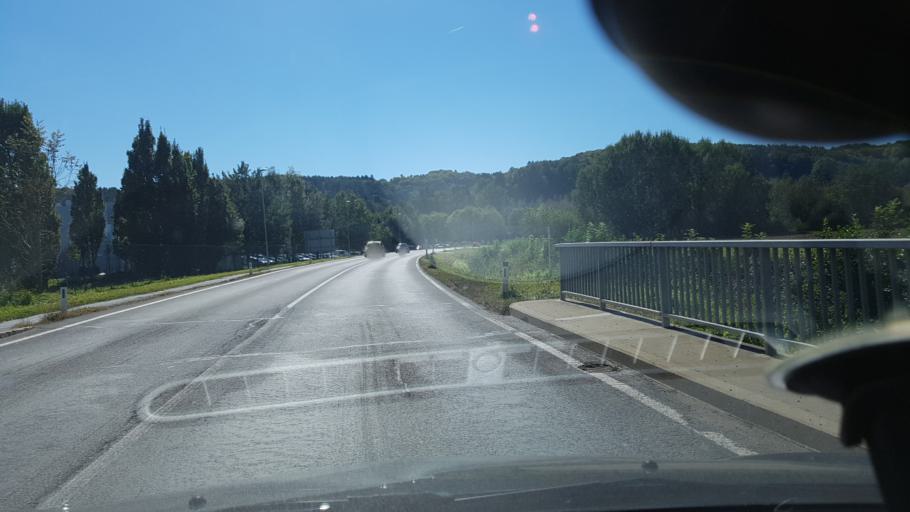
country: AT
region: Styria
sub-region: Politischer Bezirk Weiz
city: Sinabelkirchen
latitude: 47.1006
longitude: 15.8198
